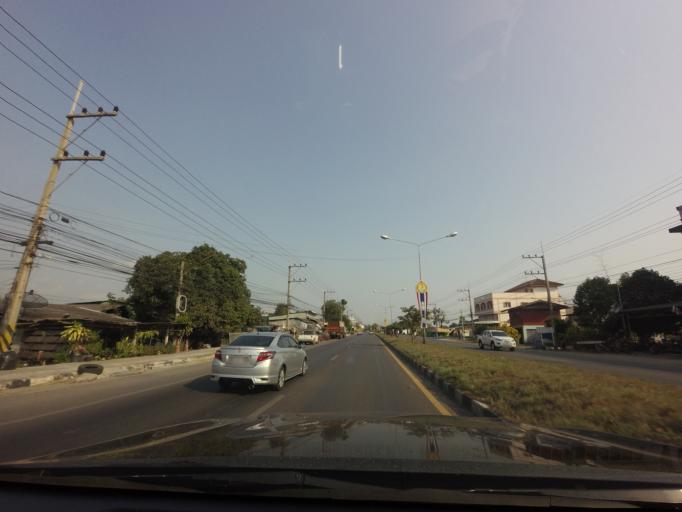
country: TH
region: Ratchaburi
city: Ban Pong
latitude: 13.8523
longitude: 99.8426
